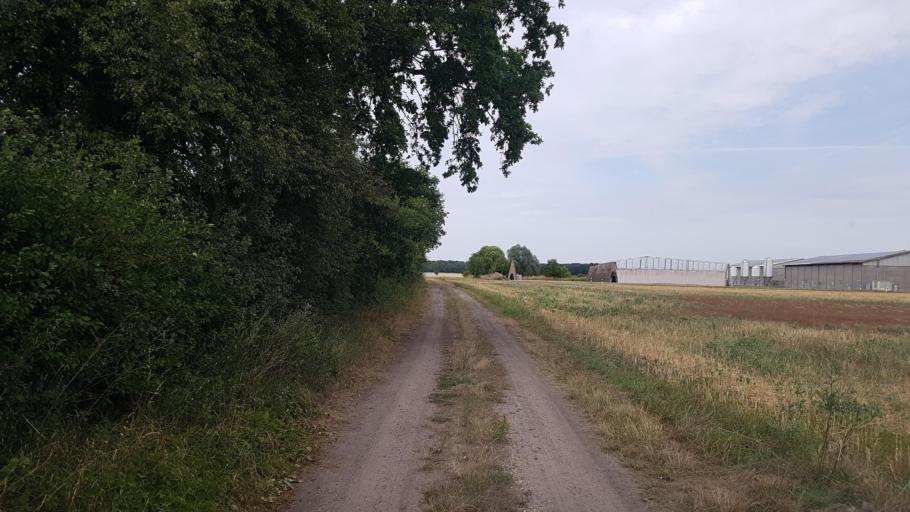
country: DE
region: Brandenburg
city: Bronkow
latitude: 51.5961
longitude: 13.9338
